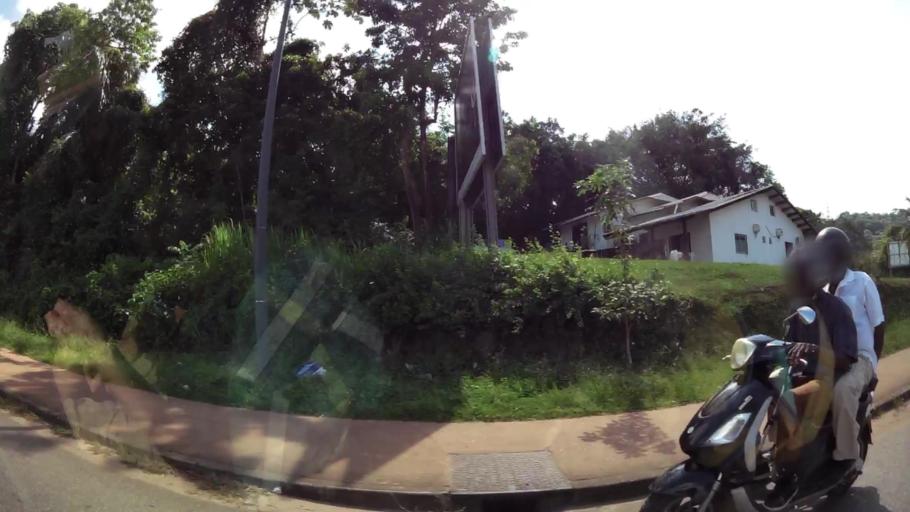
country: GF
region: Guyane
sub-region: Guyane
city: Cayenne
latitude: 4.9159
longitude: -52.3117
